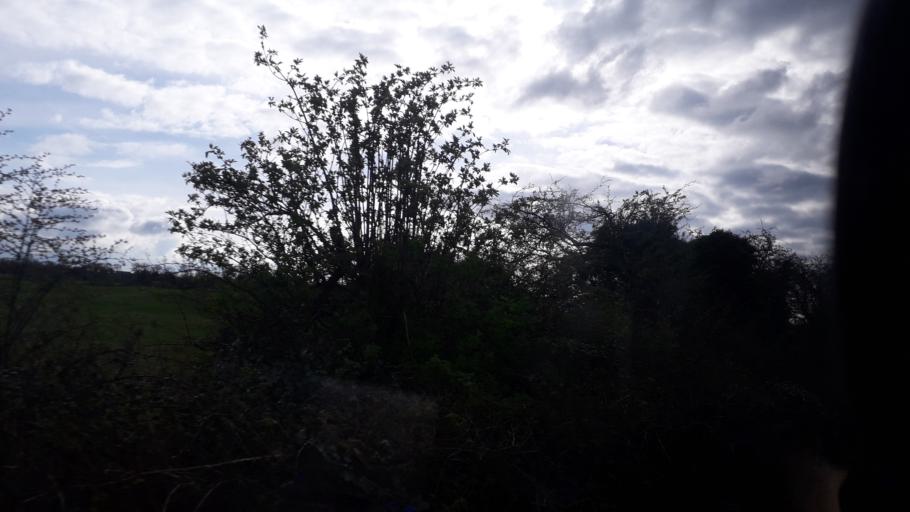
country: IE
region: Leinster
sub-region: An Iarmhi
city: An Muileann gCearr
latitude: 53.5067
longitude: -7.2938
